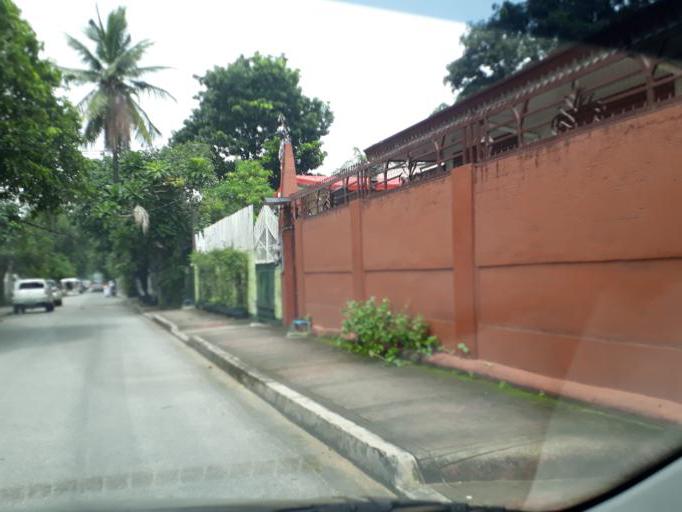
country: PH
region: Metro Manila
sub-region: Quezon City
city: Quezon City
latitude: 14.6322
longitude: 121.0544
